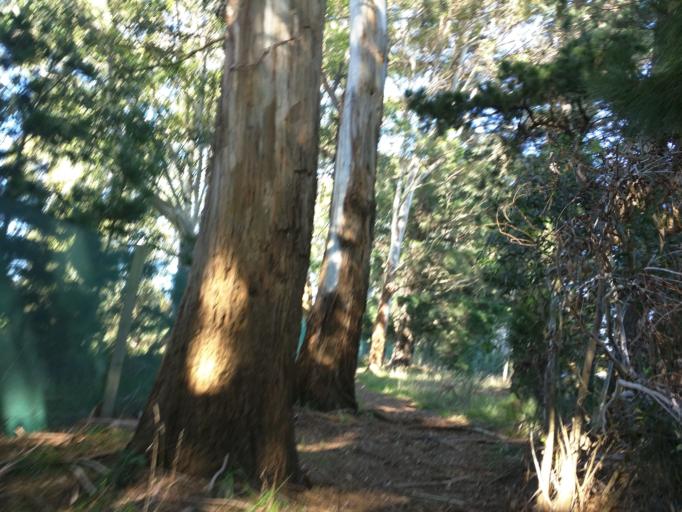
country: NZ
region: Canterbury
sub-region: Selwyn District
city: Lincoln
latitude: -43.6439
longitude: 172.4579
